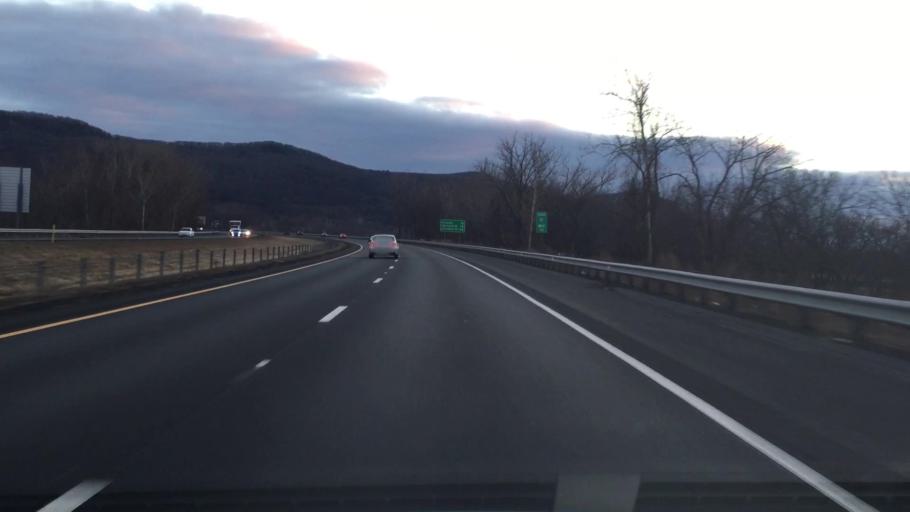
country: US
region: Massachusetts
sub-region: Hampshire County
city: Northampton
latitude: 42.2973
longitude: -72.6300
